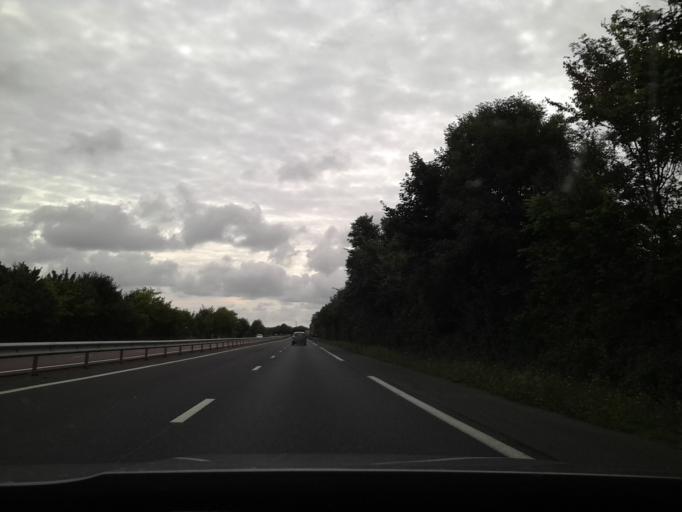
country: FR
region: Lower Normandy
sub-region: Departement du Calvados
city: Grandcamp-Maisy
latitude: 49.3427
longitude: -1.0394
